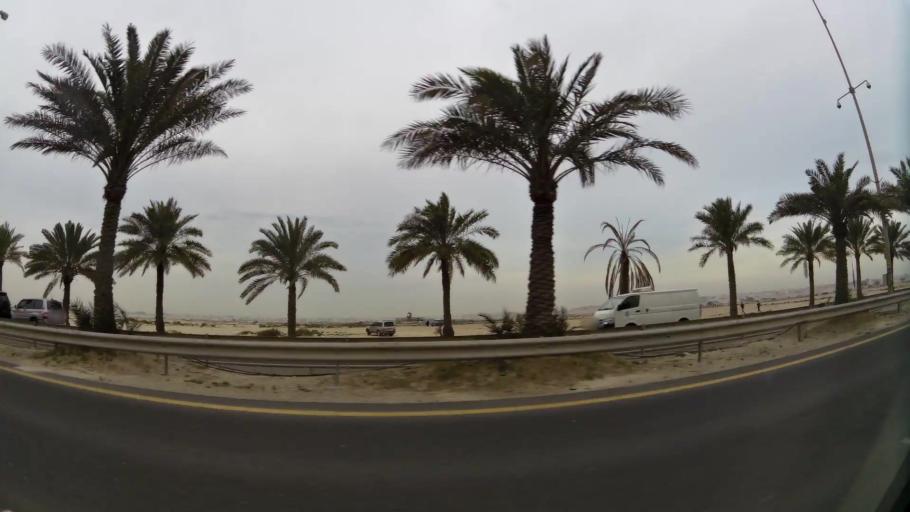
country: BH
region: Northern
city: Ar Rifa'
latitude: 26.1023
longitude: 50.5590
